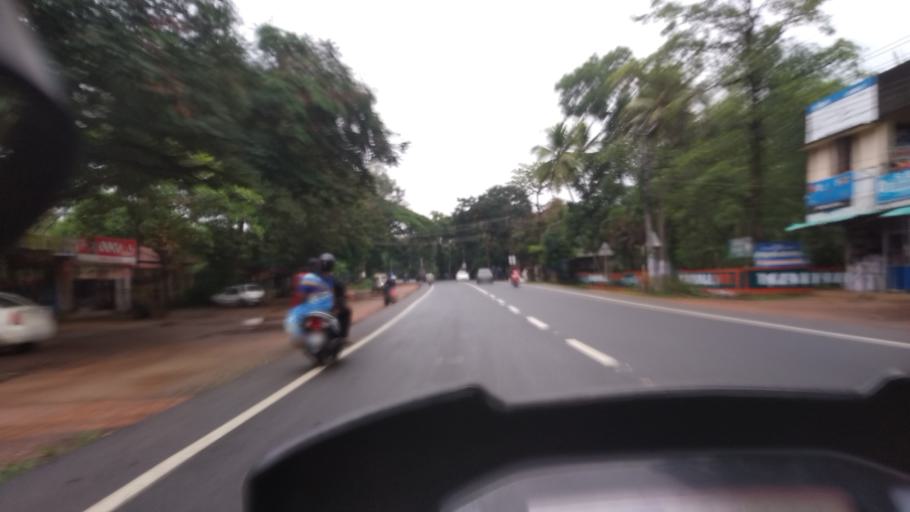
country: IN
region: Kerala
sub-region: Alappuzha
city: Mavelikara
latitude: 9.3075
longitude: 76.4318
